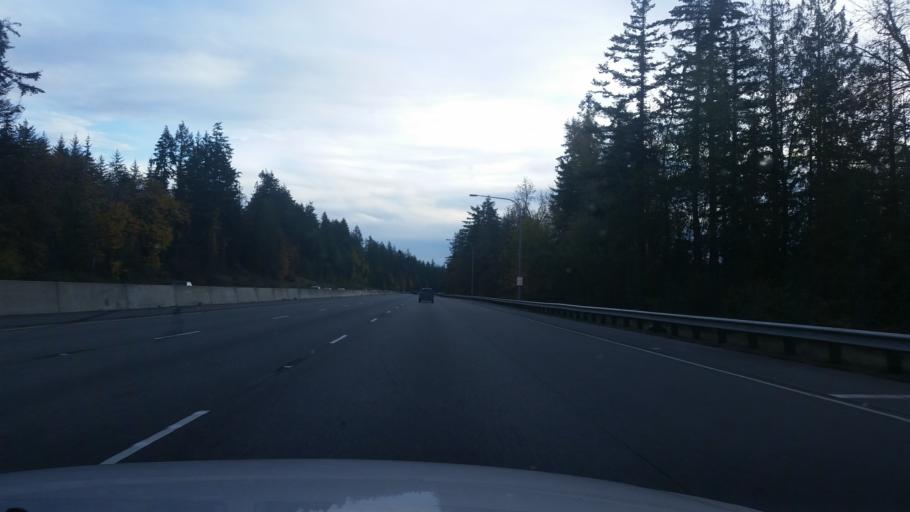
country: US
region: Washington
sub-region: Thurston County
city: Grand Mound
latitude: 46.8654
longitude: -122.9711
